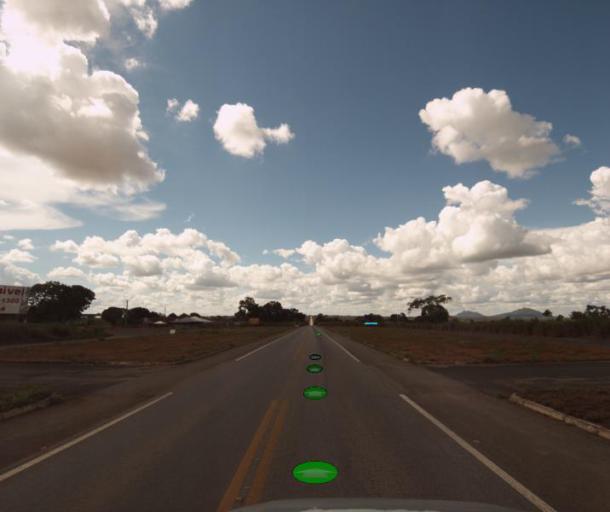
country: BR
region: Goias
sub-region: Porangatu
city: Porangatu
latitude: -13.4839
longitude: -49.1364
